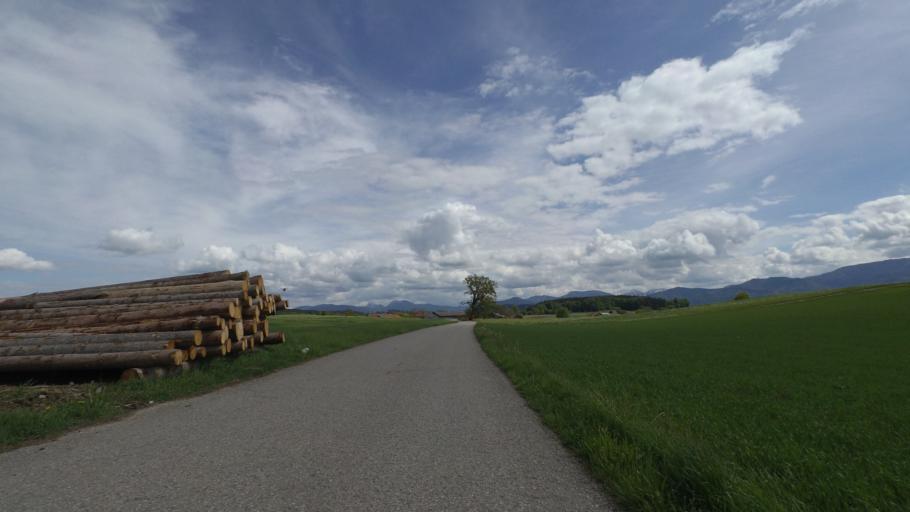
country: DE
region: Bavaria
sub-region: Upper Bavaria
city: Grabenstatt
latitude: 47.8673
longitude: 12.5737
